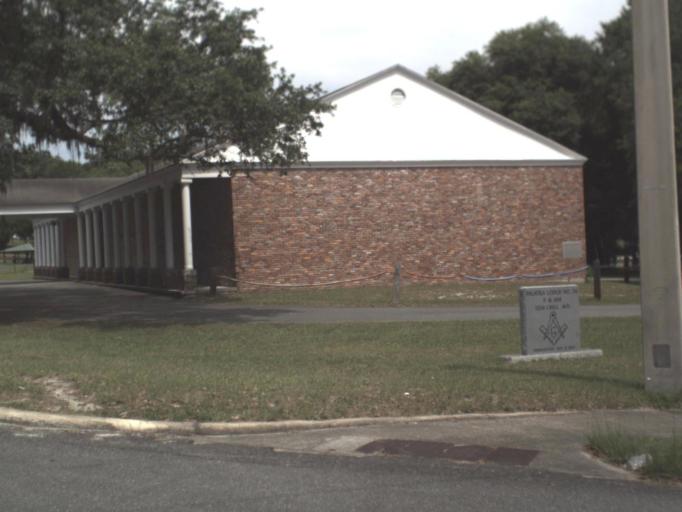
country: US
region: Florida
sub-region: Putnam County
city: Palatka
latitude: 29.6435
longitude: -81.6434
